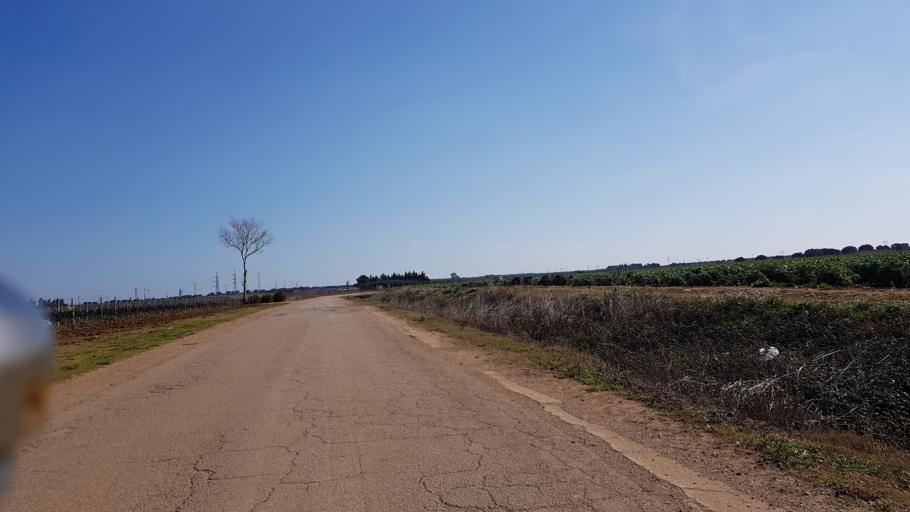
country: IT
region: Apulia
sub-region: Provincia di Brindisi
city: Mesagne
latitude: 40.6212
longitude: 17.8078
